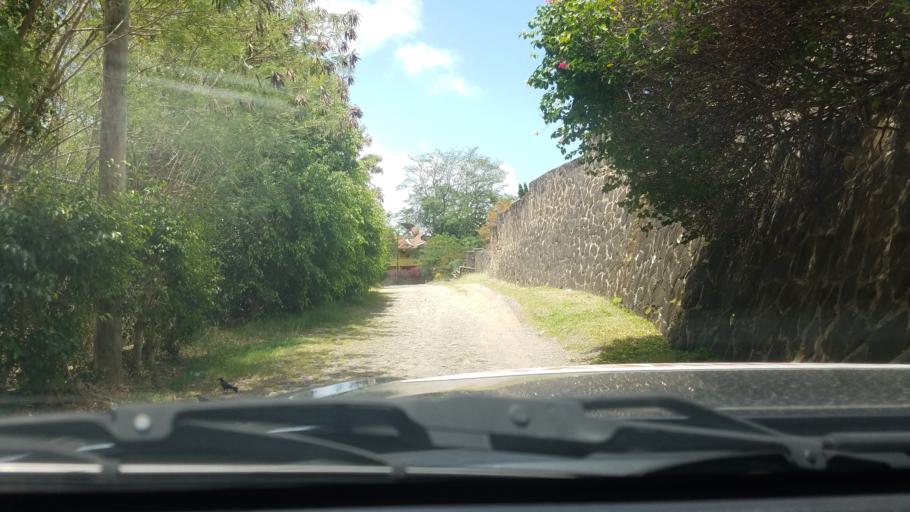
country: LC
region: Gros-Islet
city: Gros Islet
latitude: 14.0704
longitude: -60.9580
